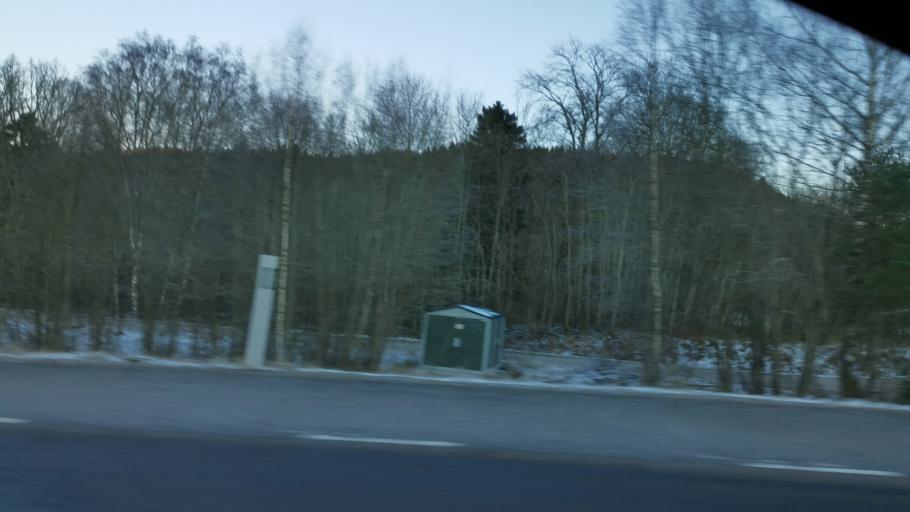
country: SE
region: Vaestra Goetaland
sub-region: Munkedals Kommun
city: Munkedal
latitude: 58.4295
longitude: 11.7221
